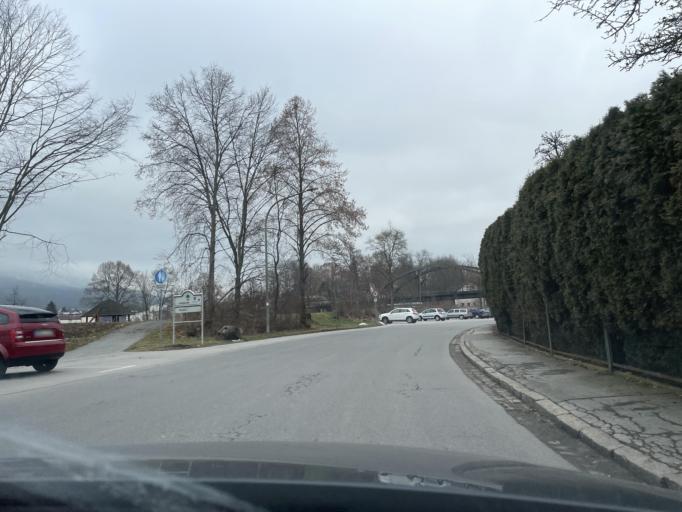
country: DE
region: Bavaria
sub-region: Upper Palatinate
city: Kotzting
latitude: 49.1734
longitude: 12.8579
